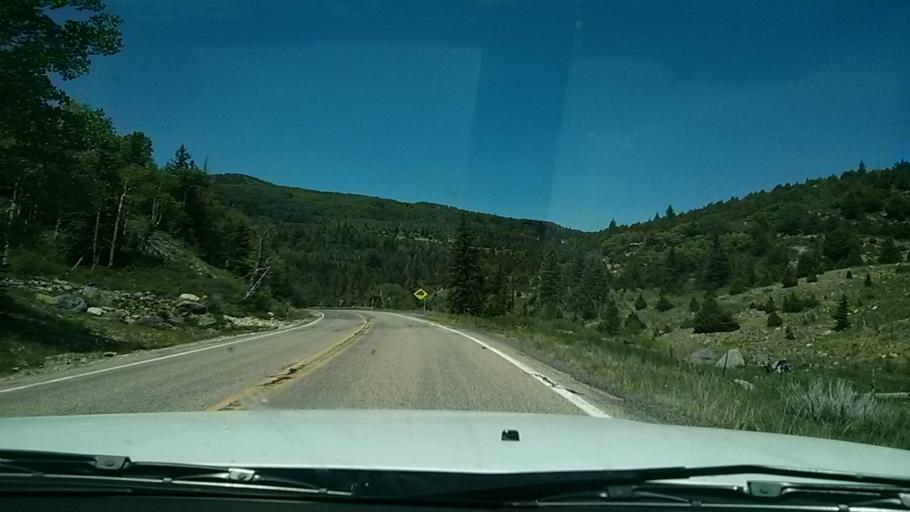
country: US
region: Utah
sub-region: Iron County
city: Cedar City
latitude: 37.5983
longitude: -112.9292
